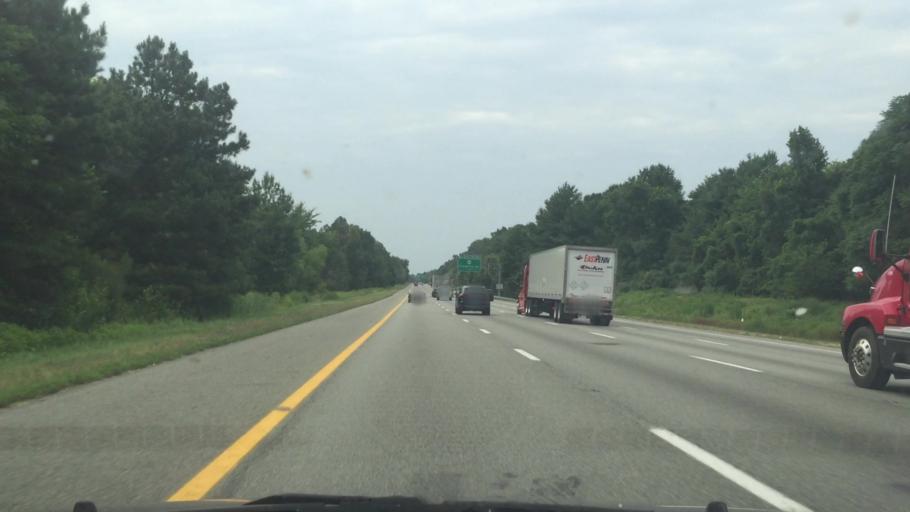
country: US
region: Virginia
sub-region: Hanover County
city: Mechanicsville
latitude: 37.5930
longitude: -77.3462
